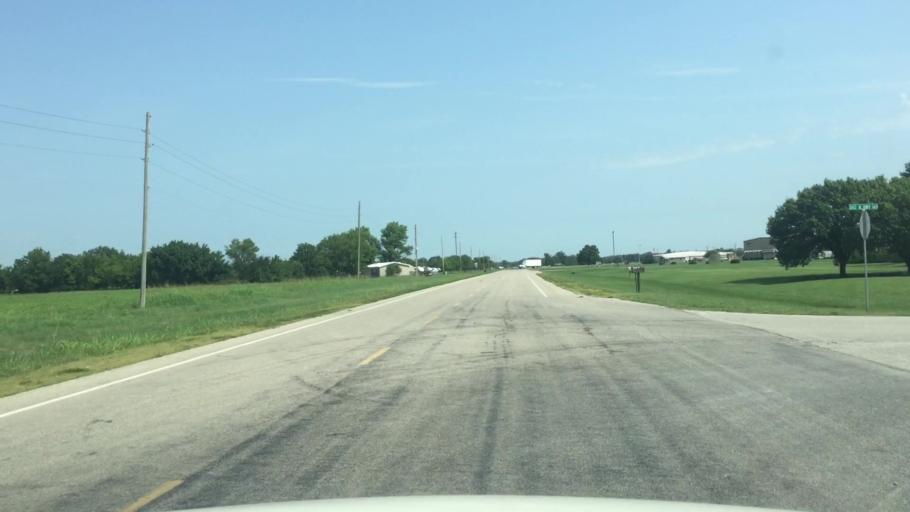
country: US
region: Kansas
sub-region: Montgomery County
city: Coffeyville
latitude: 37.0950
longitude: -95.5861
